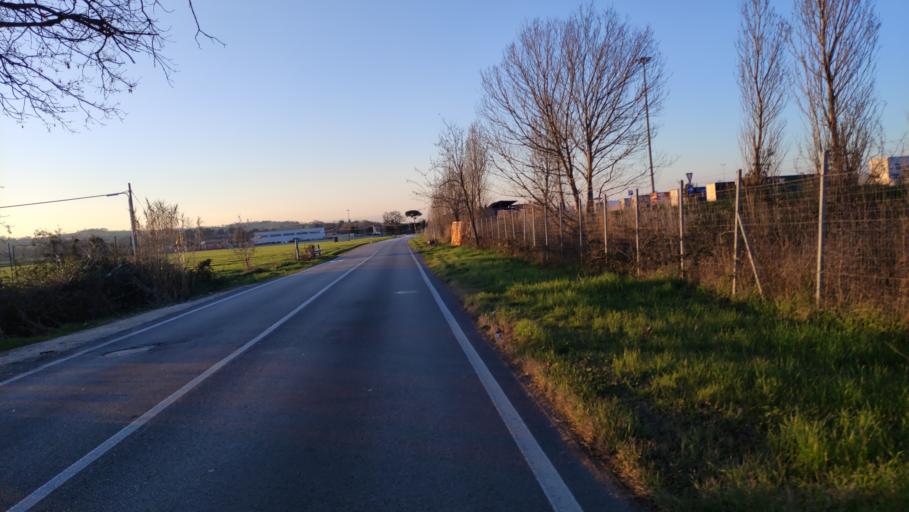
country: IT
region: The Marches
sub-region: Provincia di Pesaro e Urbino
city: Marotta
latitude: 43.7522
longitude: 13.1458
